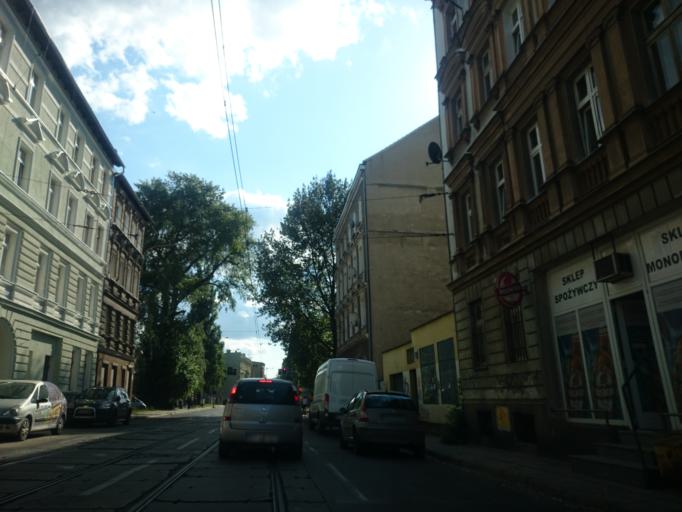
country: PL
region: West Pomeranian Voivodeship
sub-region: Szczecin
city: Szczecin
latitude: 53.4152
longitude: 14.5471
